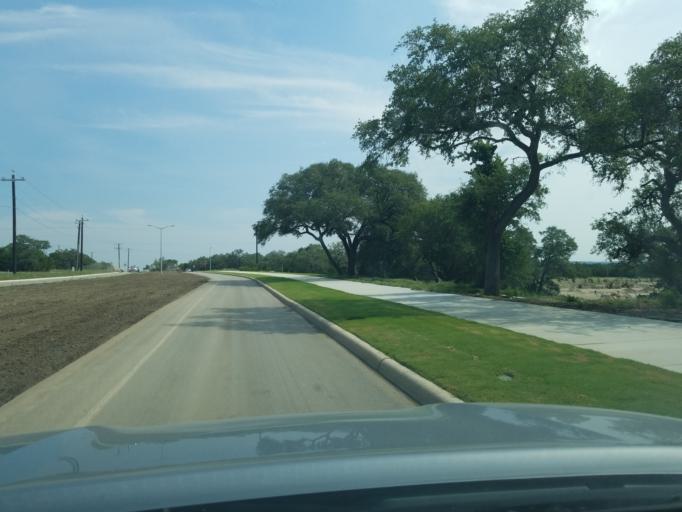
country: US
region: Texas
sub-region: Kendall County
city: Boerne
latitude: 29.7544
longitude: -98.7190
